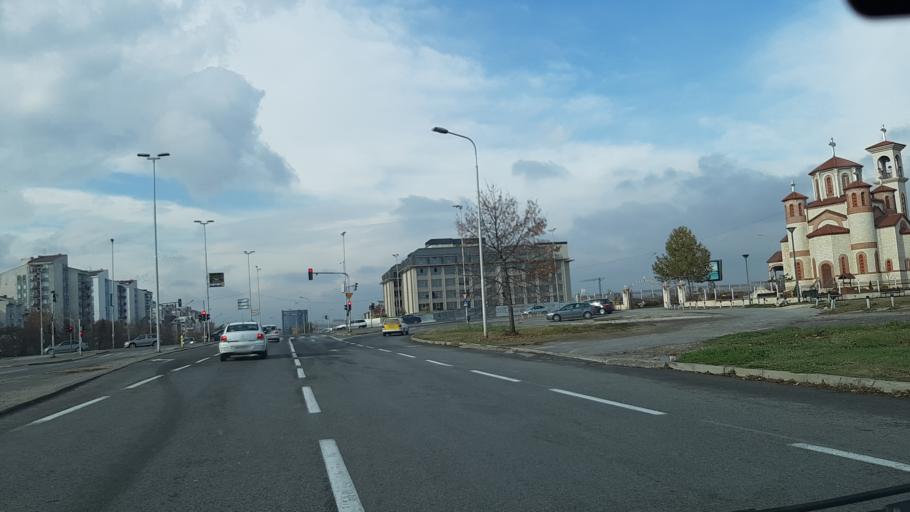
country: MK
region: Kisela Voda
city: Usje
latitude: 41.9892
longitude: 21.4751
